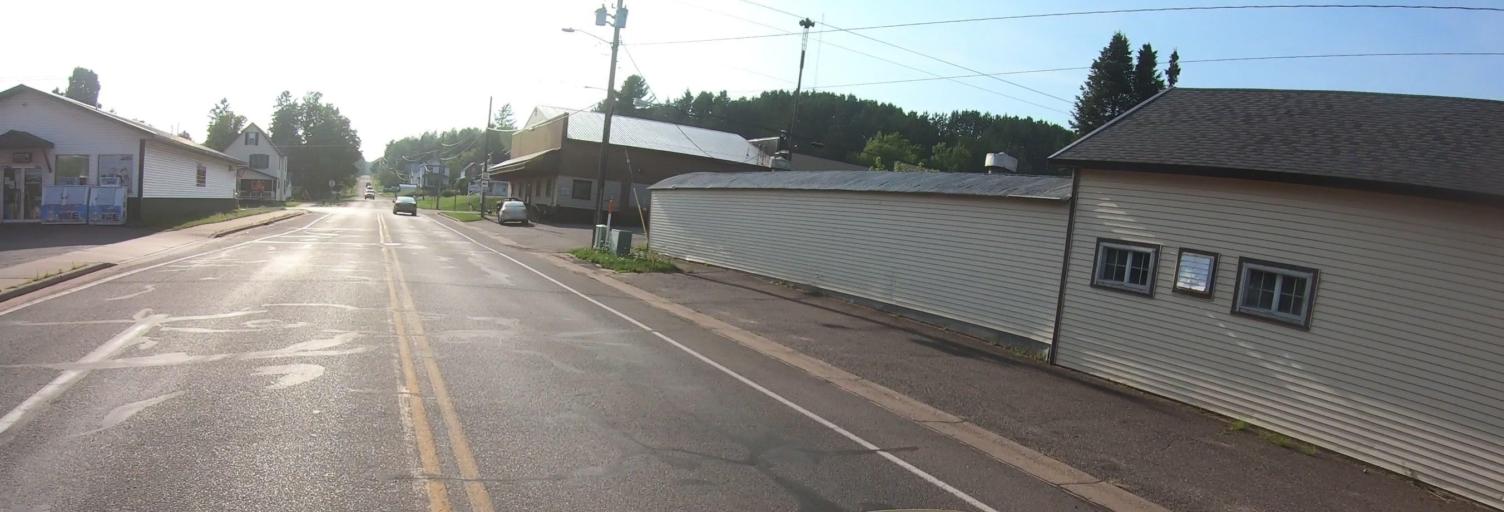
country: US
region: Wisconsin
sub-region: Ashland County
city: Ashland
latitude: 46.3257
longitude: -90.6608
